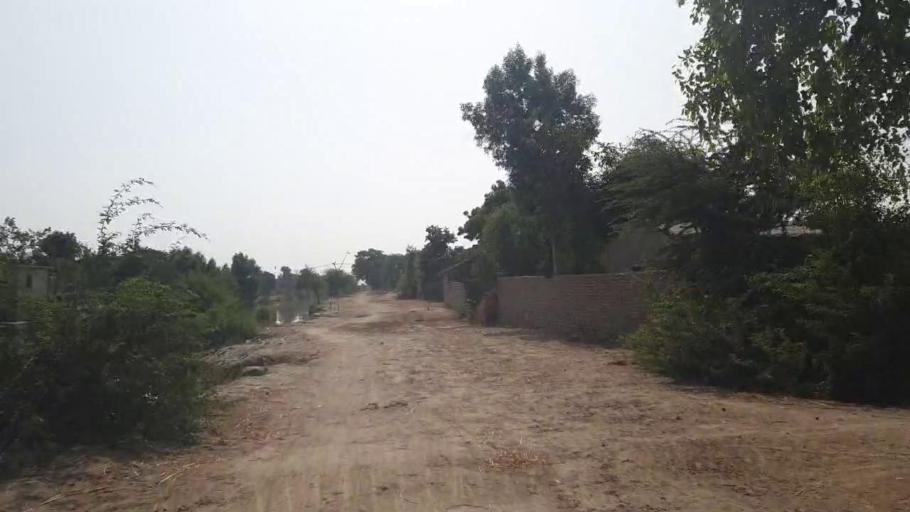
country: PK
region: Sindh
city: Badin
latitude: 24.6510
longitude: 68.8446
